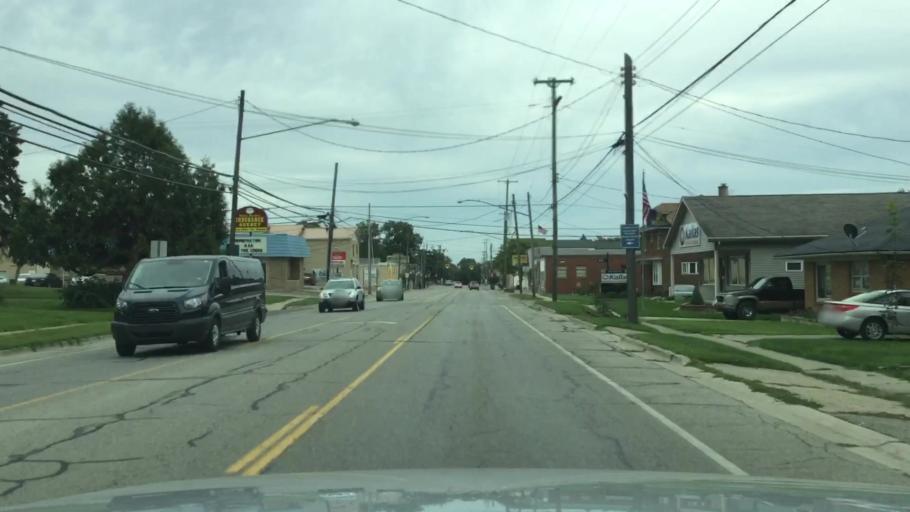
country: US
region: Michigan
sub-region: Genesee County
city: Swartz Creek
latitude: 42.9572
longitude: -83.8342
